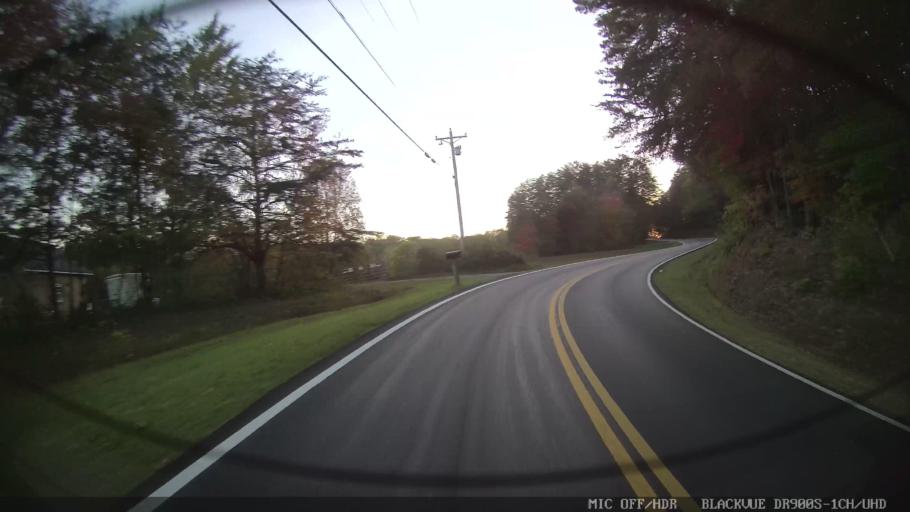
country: US
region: Georgia
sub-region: Union County
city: Blairsville
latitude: 34.8539
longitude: -83.9043
